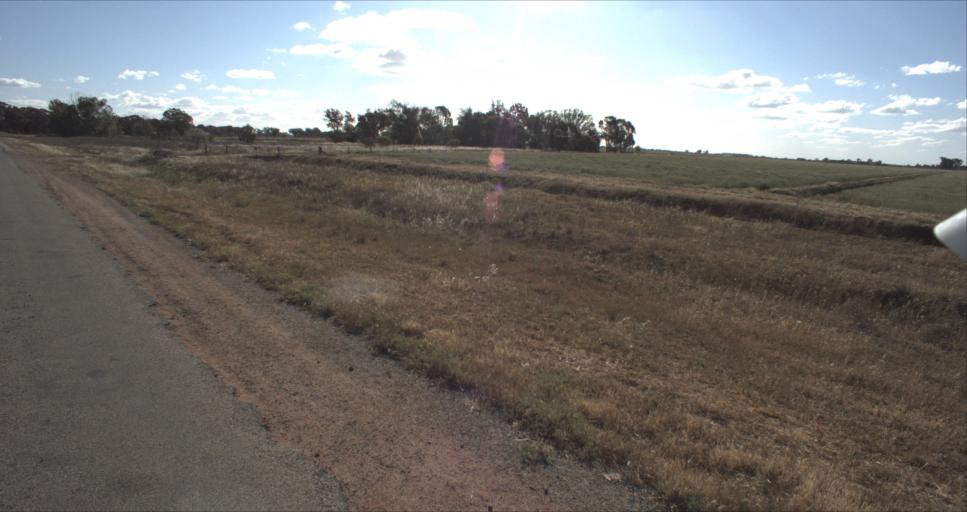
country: AU
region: New South Wales
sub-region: Leeton
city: Leeton
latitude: -34.4565
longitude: 146.2728
